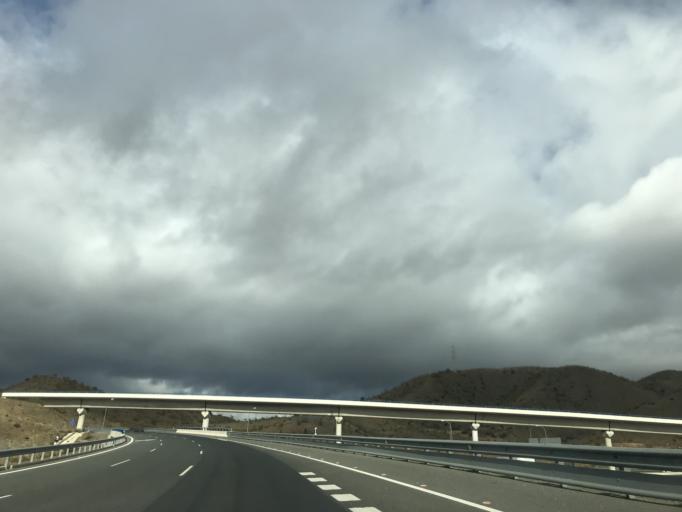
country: ES
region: Andalusia
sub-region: Provincia de Malaga
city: Malaga
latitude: 36.7554
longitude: -4.4841
